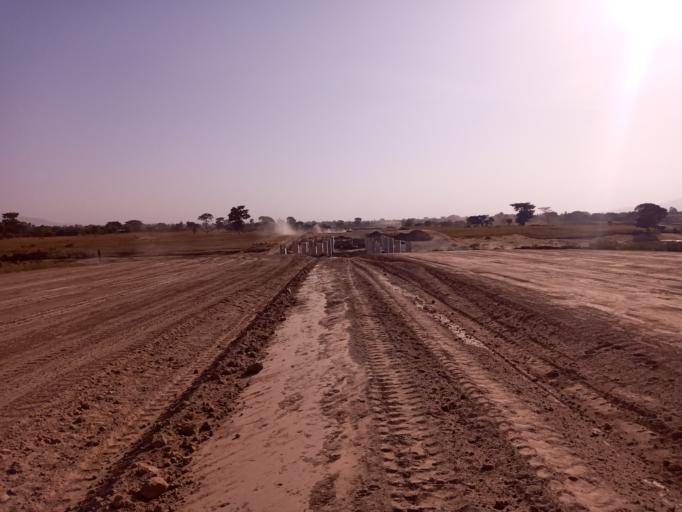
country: ET
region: Oromiya
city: Shashemene
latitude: 7.2898
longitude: 38.6109
